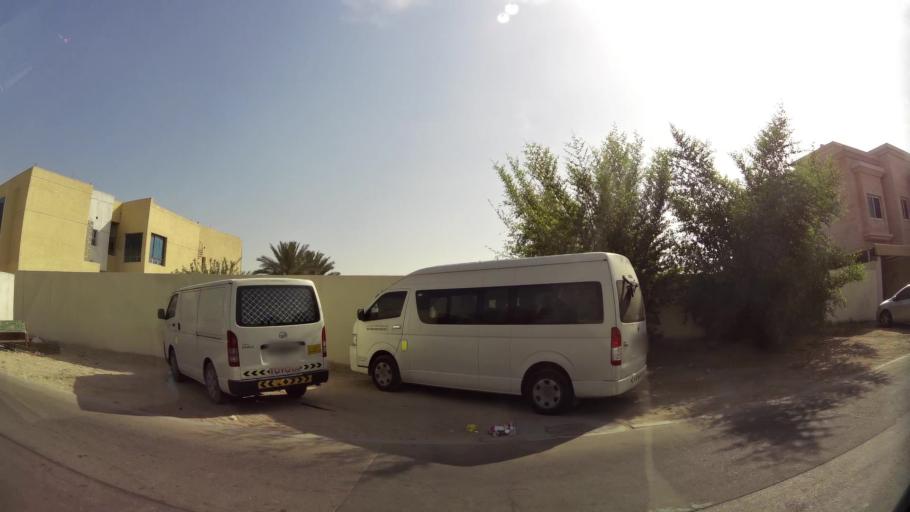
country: AE
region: Ash Shariqah
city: Sharjah
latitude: 25.2631
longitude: 55.4019
